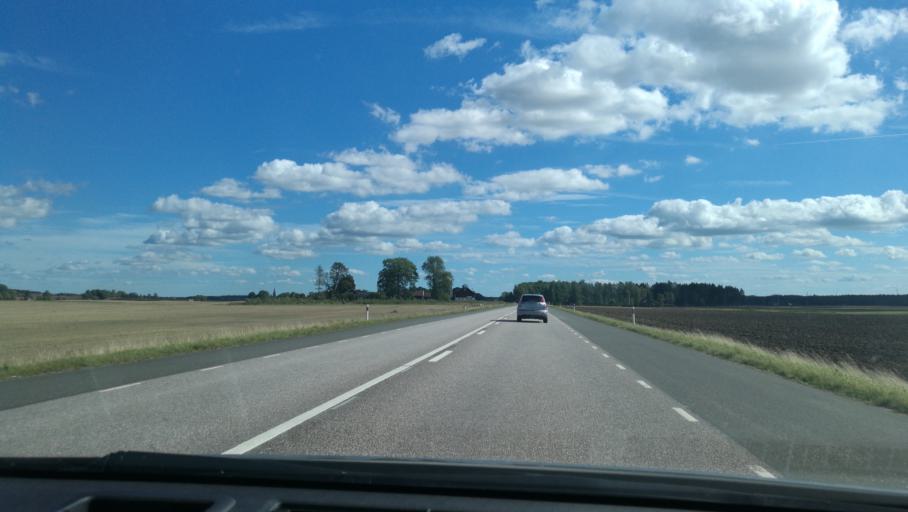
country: SE
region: Vaestra Goetaland
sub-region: Gotene Kommun
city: Kallby
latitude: 58.5095
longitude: 13.3777
